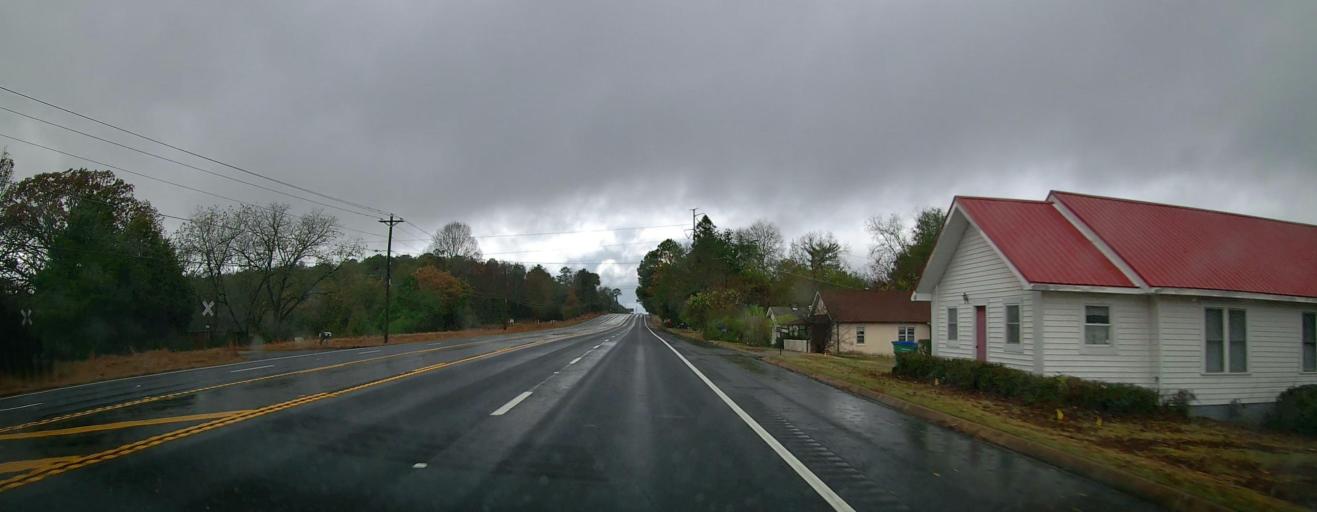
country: US
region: Georgia
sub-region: Clarke County
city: Country Club Estates
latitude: 34.0180
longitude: -83.3914
